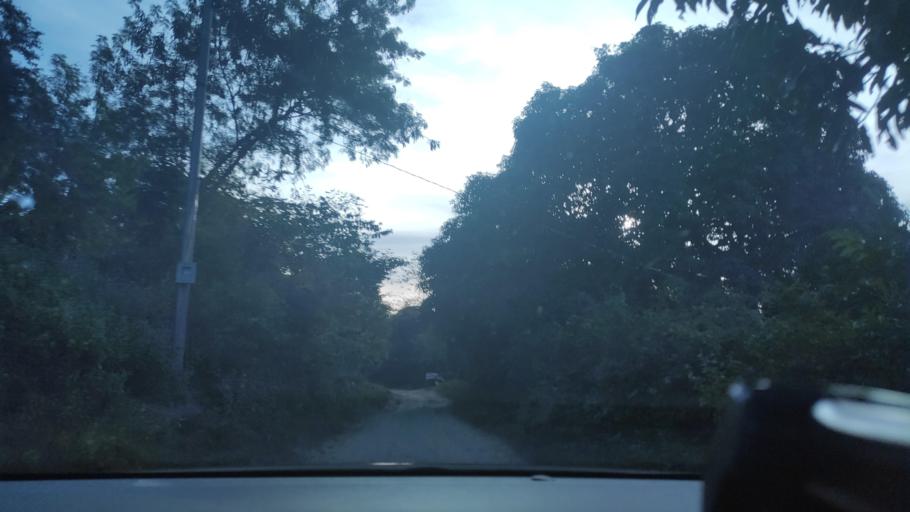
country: PH
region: Ilocos
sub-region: Province of Pangasinan
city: Balingasay
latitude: 16.3092
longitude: 119.8645
